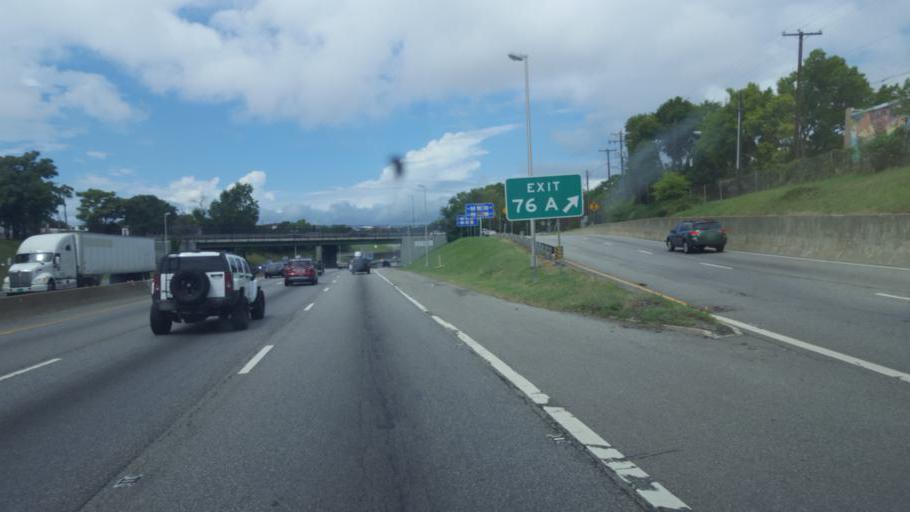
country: US
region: Virginia
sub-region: City of Richmond
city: Richmond
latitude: 37.5512
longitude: -77.4391
